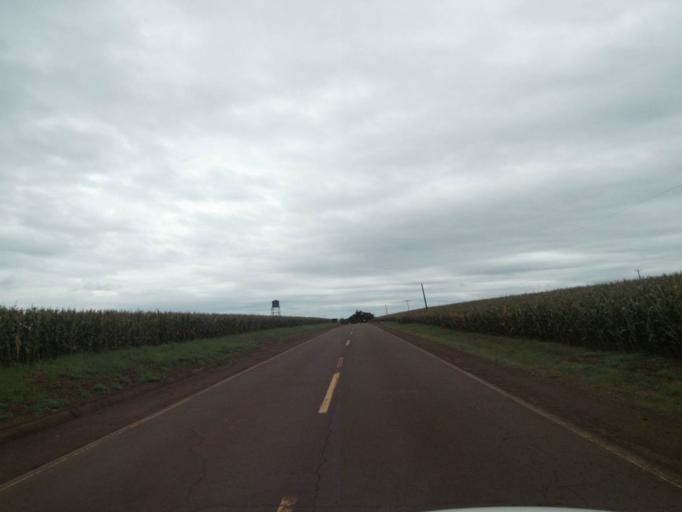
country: BR
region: Parana
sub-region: Marechal Candido Rondon
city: Marechal Candido Rondon
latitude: -24.8018
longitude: -54.2040
